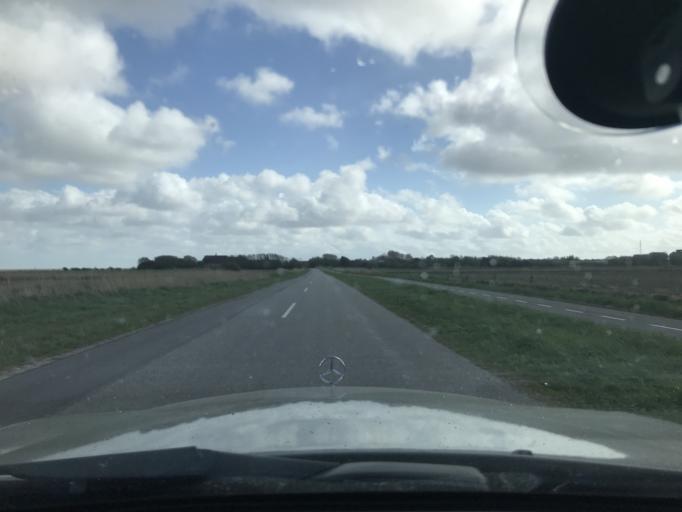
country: DE
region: Schleswig-Holstein
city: List
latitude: 55.1702
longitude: 8.5555
